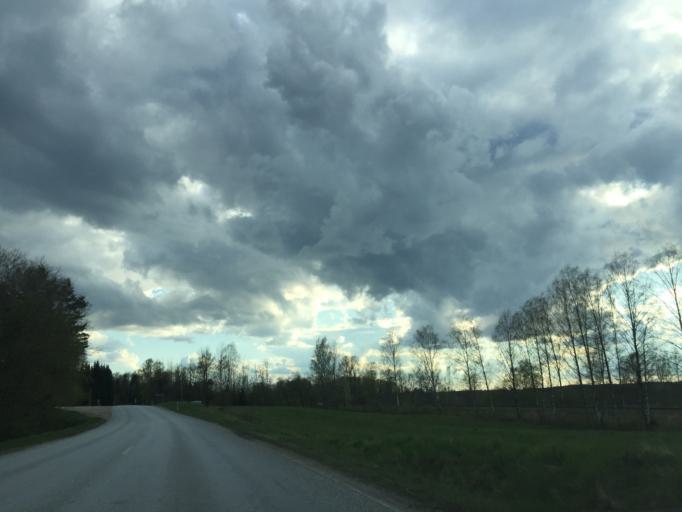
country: LV
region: Priekuli
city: Priekuli
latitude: 57.3465
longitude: 25.3446
